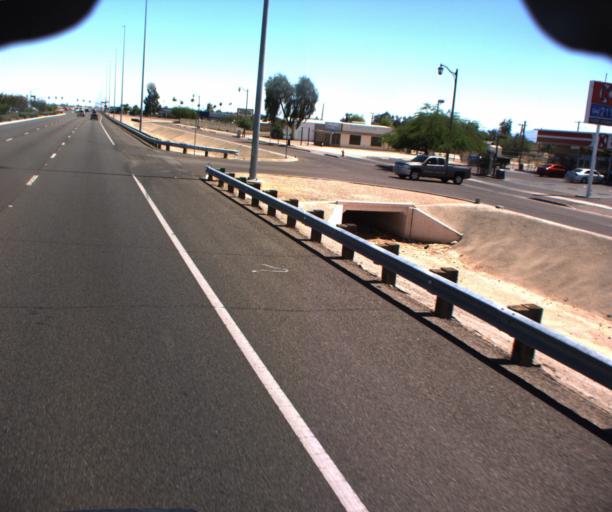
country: US
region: Arizona
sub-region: Maricopa County
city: Surprise
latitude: 33.6259
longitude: -112.3340
